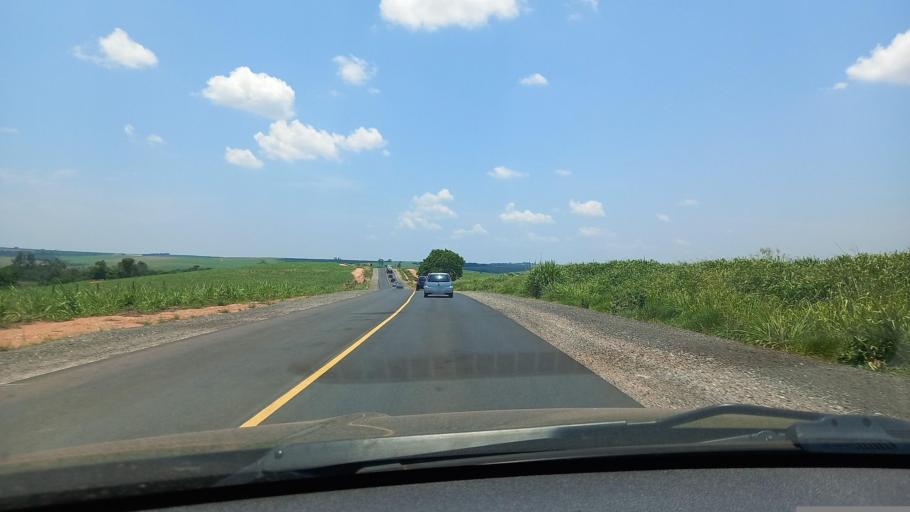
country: BR
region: Sao Paulo
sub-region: Moji-Guacu
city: Mogi-Gaucu
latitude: -22.3674
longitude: -46.8732
